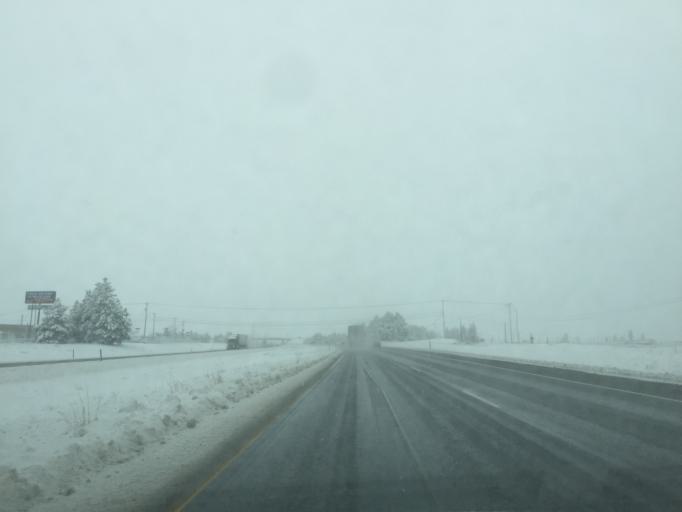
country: US
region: Washington
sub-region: Spokane County
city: Airway Heights
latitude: 47.5963
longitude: -117.5575
